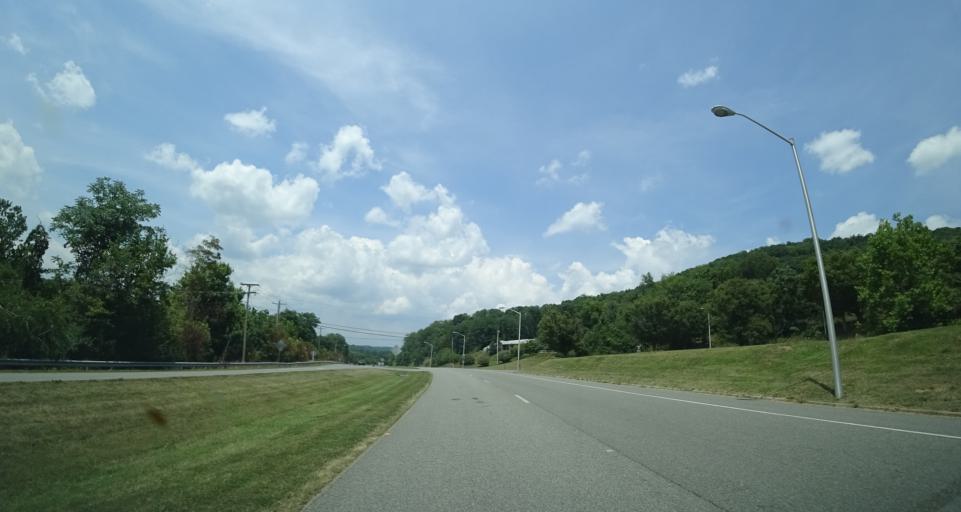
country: US
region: Virginia
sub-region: City of Radford
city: Radford
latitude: 37.0948
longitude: -80.5788
